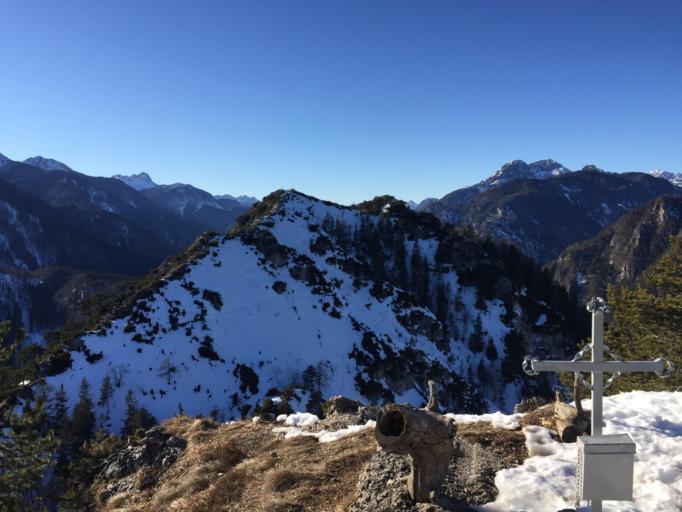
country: IT
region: Friuli Venezia Giulia
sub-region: Provincia di Udine
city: Malborghetto
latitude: 46.5029
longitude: 13.4706
